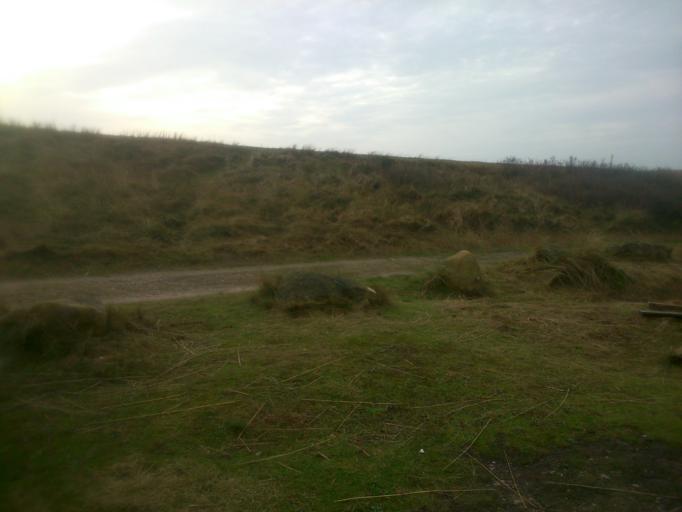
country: DK
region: Central Jutland
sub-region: Ringkobing-Skjern Kommune
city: Hvide Sande
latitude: 55.8188
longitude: 8.1841
